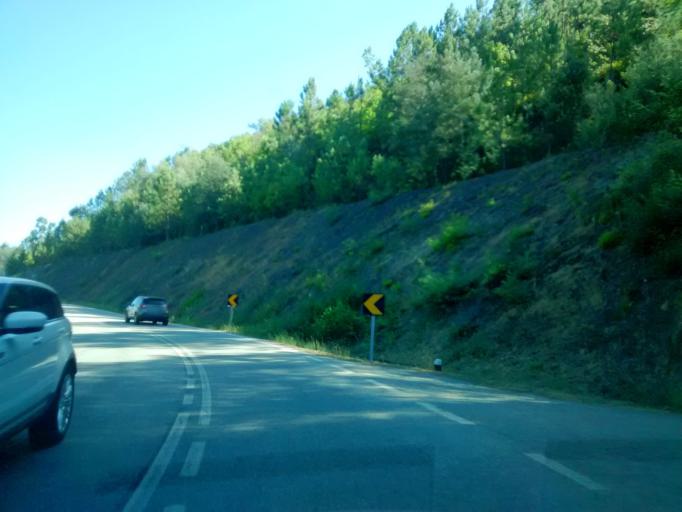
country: PT
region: Castelo Branco
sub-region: Belmonte
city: Belmonte
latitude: 40.4003
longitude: -7.3974
